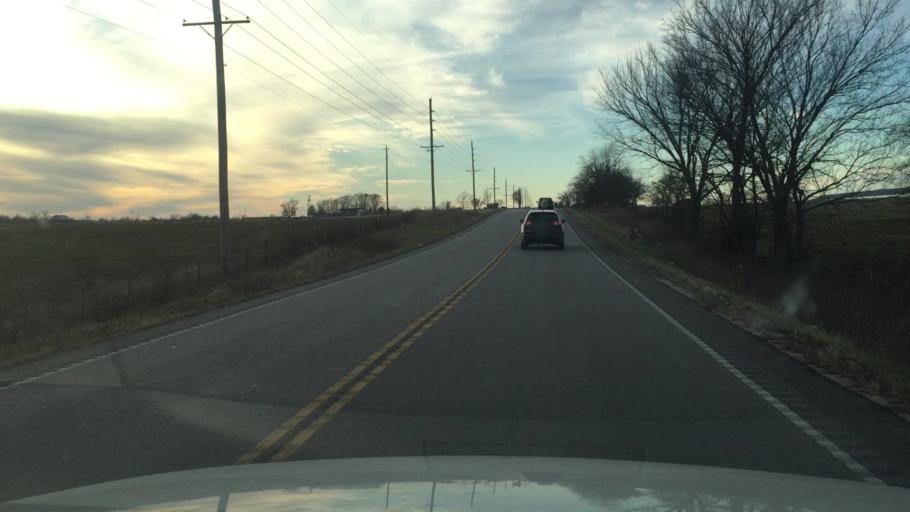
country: US
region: Missouri
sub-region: Miller County
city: Eldon
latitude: 38.3737
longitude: -92.6341
